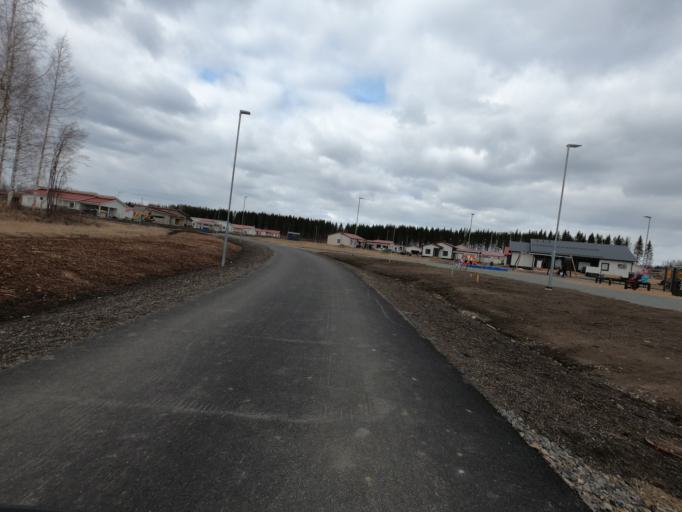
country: FI
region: North Karelia
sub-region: Joensuu
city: Joensuu
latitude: 62.5577
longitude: 29.8259
